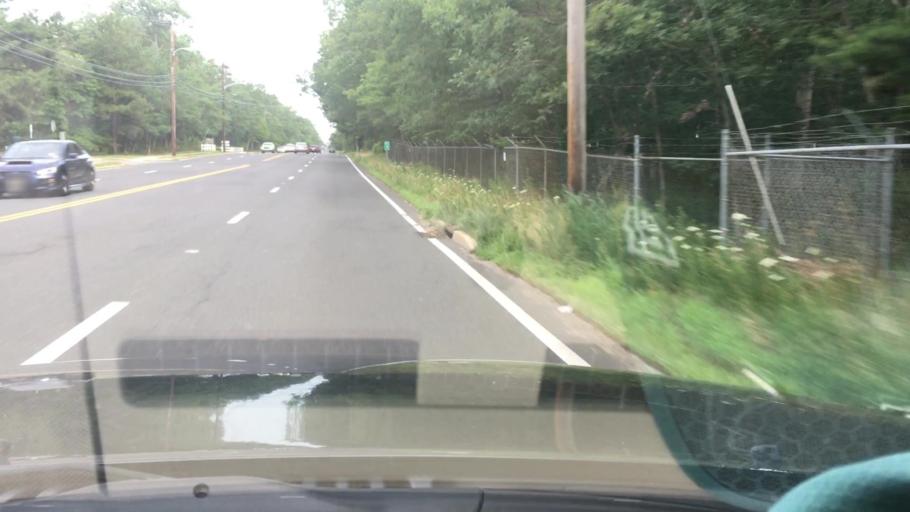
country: US
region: New Jersey
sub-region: Ocean County
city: Pine Lake Park
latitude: 40.0139
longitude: -74.2532
